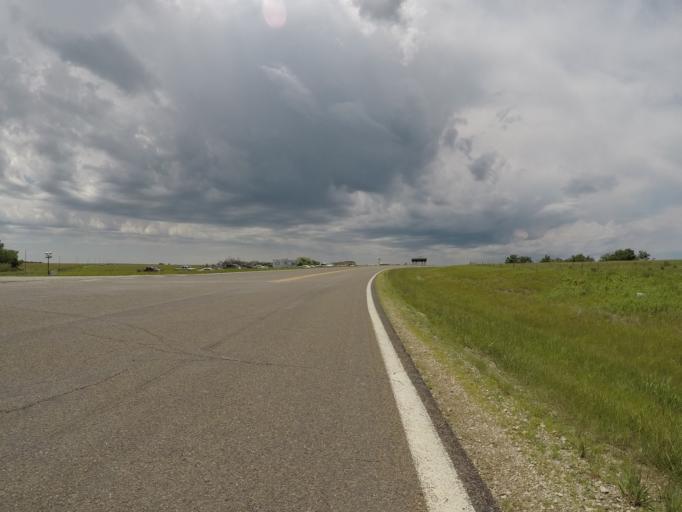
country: US
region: Kansas
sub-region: Wabaunsee County
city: Alma
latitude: 38.8571
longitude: -96.3733
